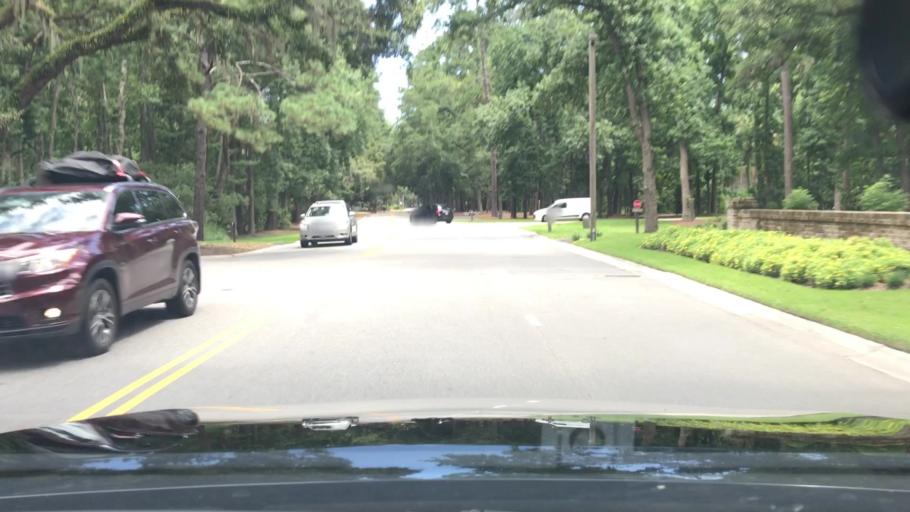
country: US
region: South Carolina
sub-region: Beaufort County
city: Hilton Head Island
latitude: 32.1353
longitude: -80.8043
